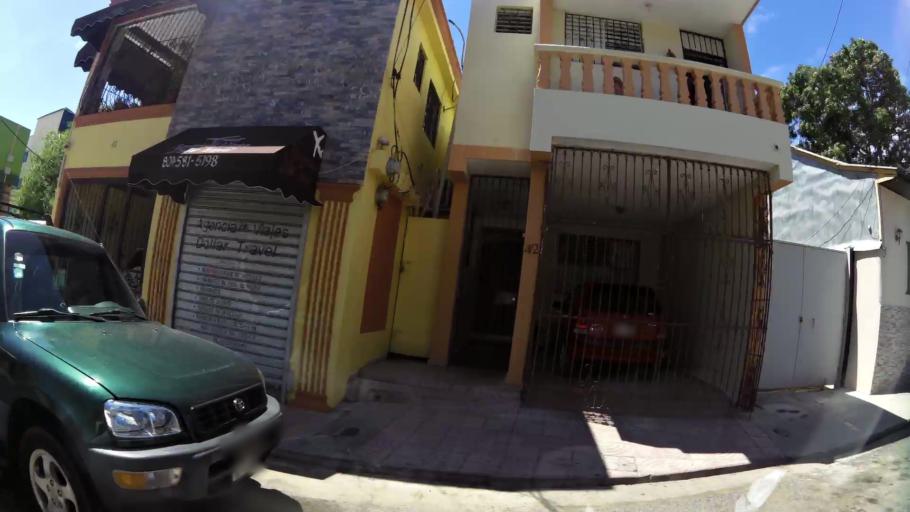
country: DO
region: Santiago
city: Santiago de los Caballeros
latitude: 19.4485
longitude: -70.6987
